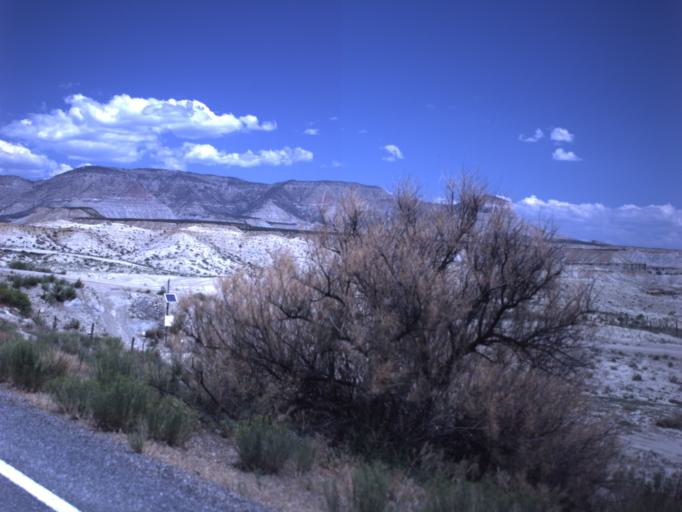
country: US
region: Utah
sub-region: Emery County
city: Orangeville
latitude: 39.2303
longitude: -111.0749
